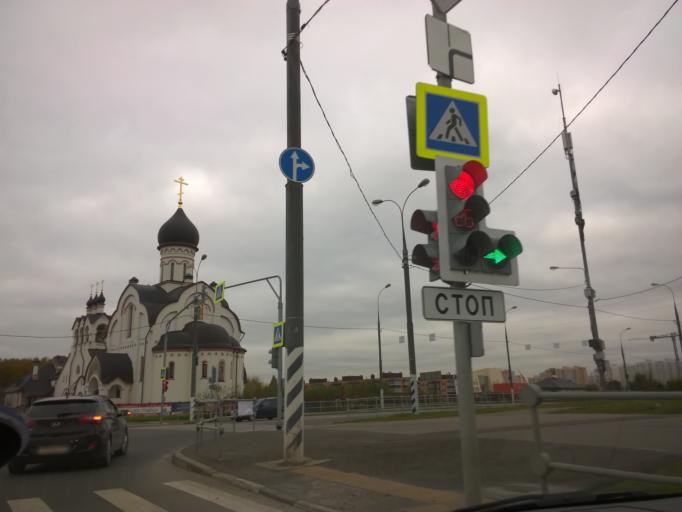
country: RU
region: Moskovskaya
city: Kommunarka
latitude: 55.5312
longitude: 37.4996
